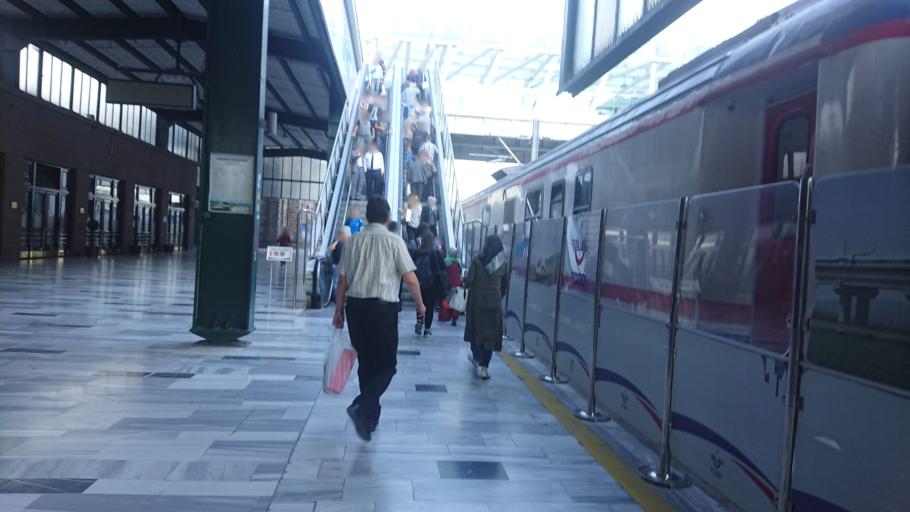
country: TR
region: Ankara
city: Ankara
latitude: 39.9357
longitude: 32.8438
